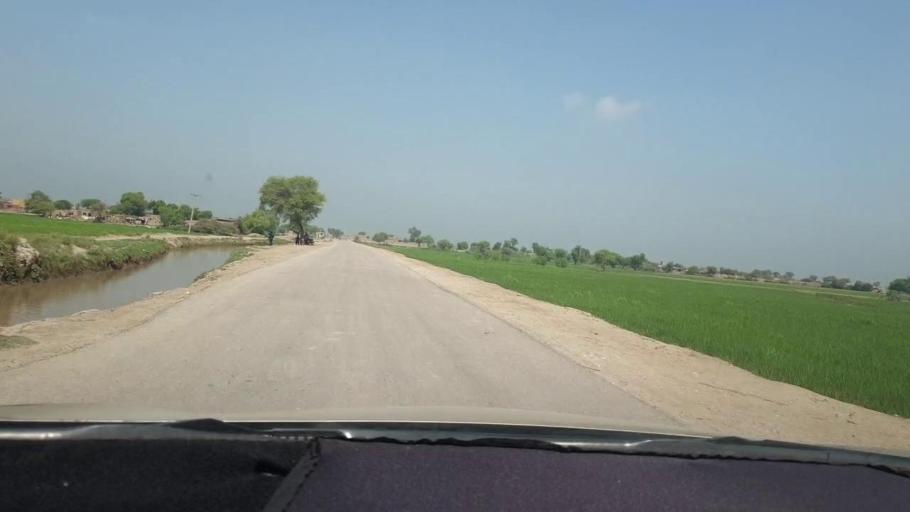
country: PK
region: Sindh
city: Miro Khan
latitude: 27.7819
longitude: 68.0534
